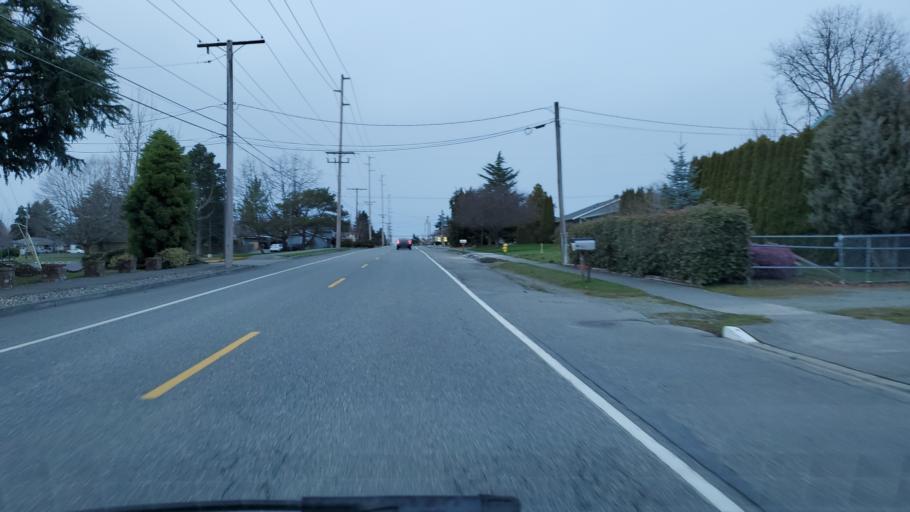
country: US
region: Washington
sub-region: Skagit County
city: Mount Vernon
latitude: 48.4107
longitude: -122.3189
